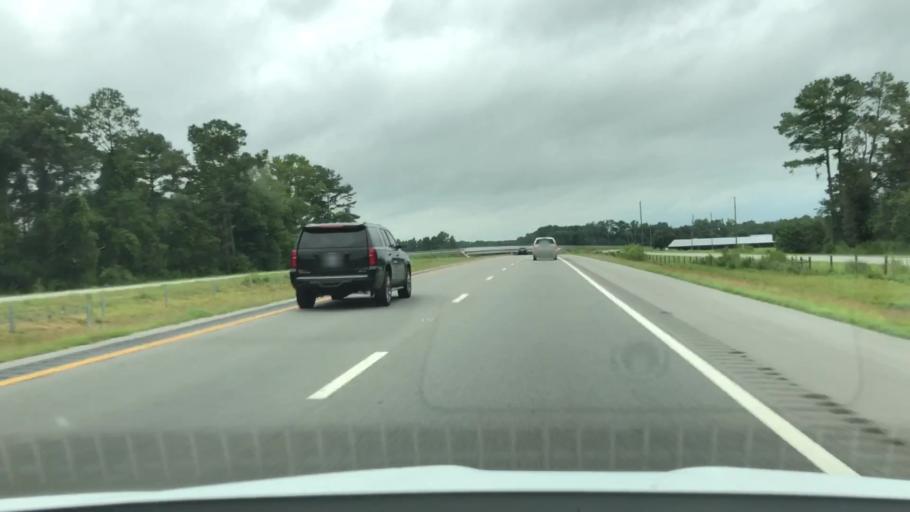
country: US
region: North Carolina
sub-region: Wayne County
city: Elroy
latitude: 35.3515
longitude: -77.8476
